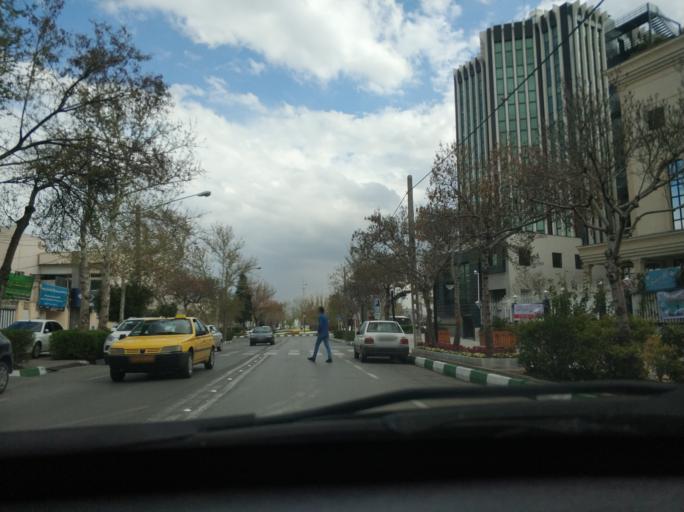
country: IR
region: Razavi Khorasan
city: Mashhad
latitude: 36.2757
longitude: 59.5910
